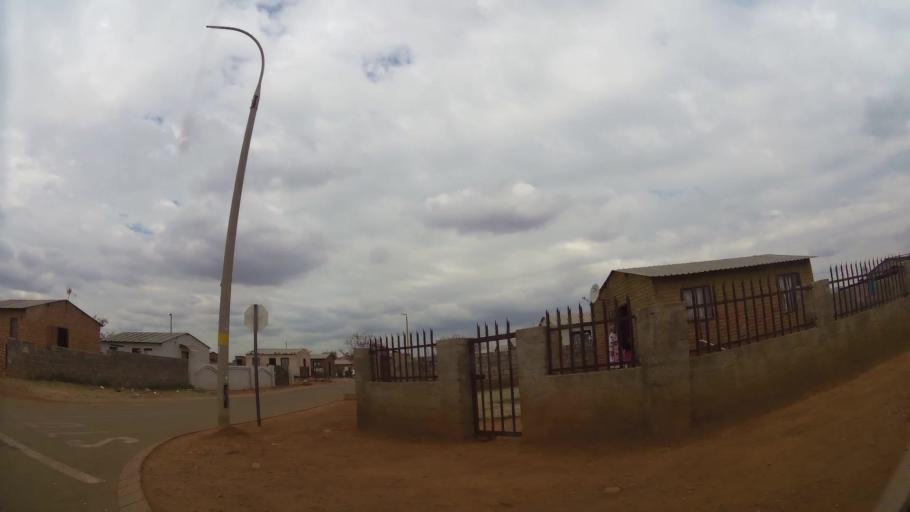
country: ZA
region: Gauteng
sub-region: Ekurhuleni Metropolitan Municipality
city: Germiston
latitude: -26.3847
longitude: 28.1193
